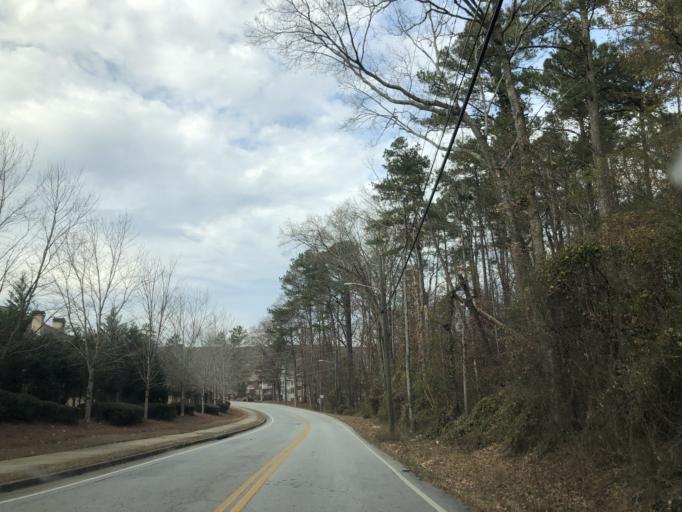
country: US
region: Georgia
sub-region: DeKalb County
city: Panthersville
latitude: 33.6644
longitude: -84.2044
